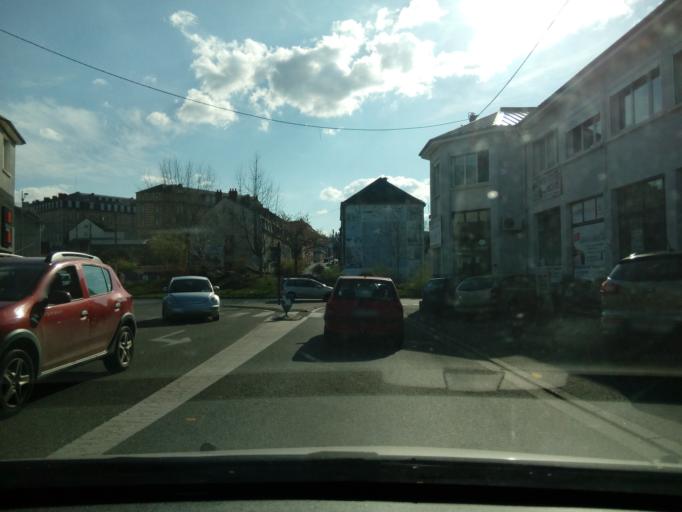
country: FR
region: Limousin
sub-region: Departement de la Creuse
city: Gueret
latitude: 46.1747
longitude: 1.8731
